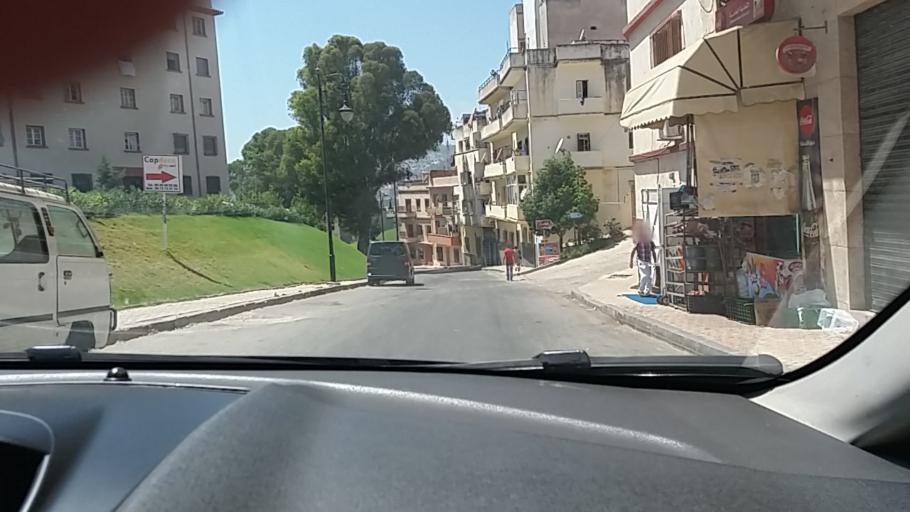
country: MA
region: Tanger-Tetouan
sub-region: Tanger-Assilah
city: Tangier
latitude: 35.7865
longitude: -5.8221
